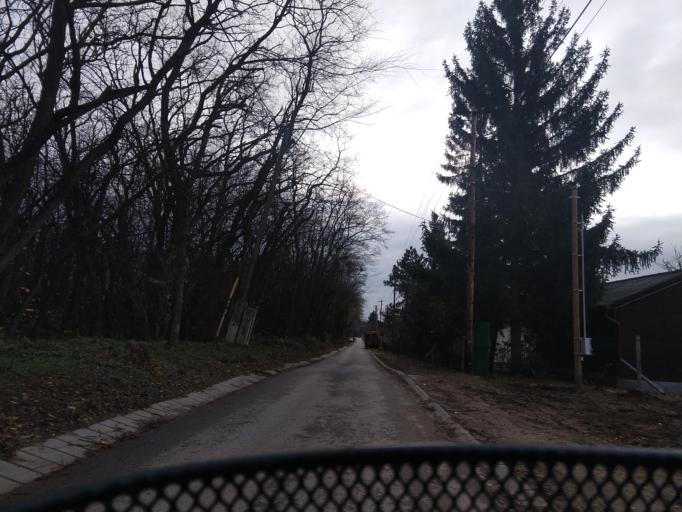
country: HU
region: Pest
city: Veresegyhaz
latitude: 47.6493
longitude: 19.2699
